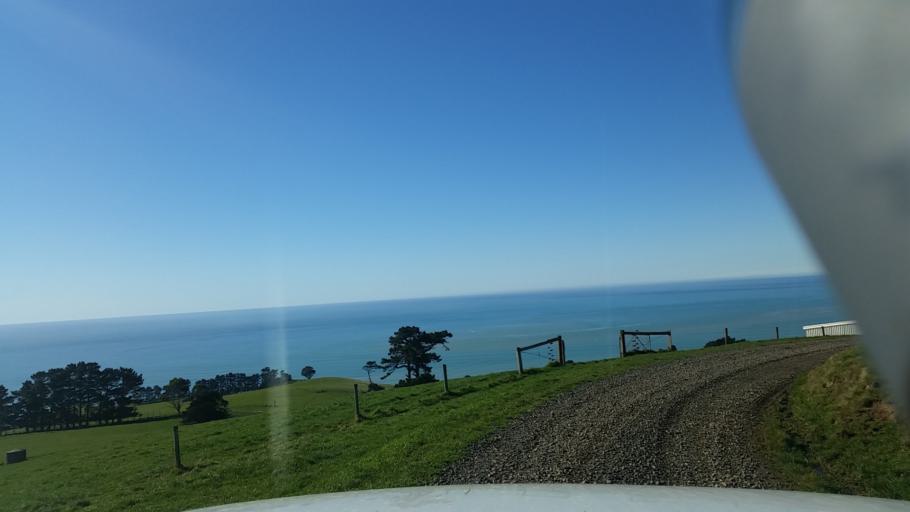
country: NZ
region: Canterbury
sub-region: Christchurch City
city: Christchurch
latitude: -43.6511
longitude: 172.9849
